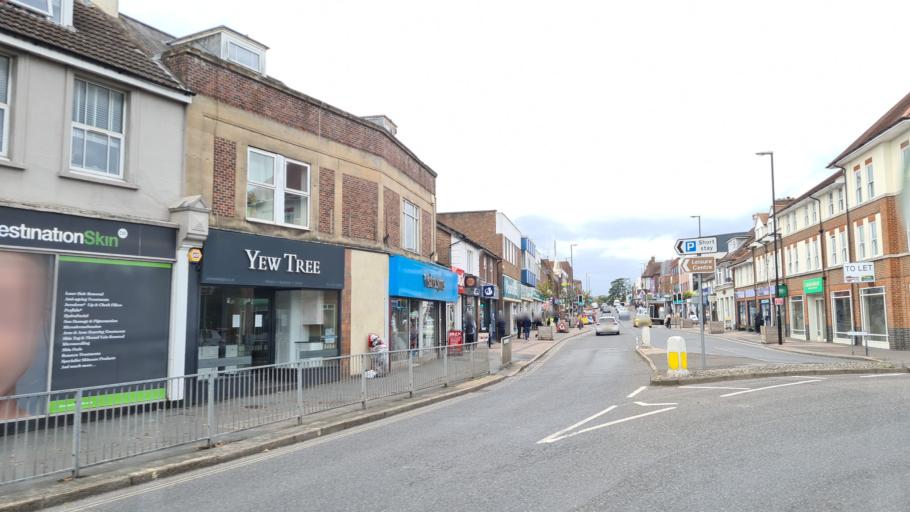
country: GB
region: England
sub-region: West Sussex
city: Haywards Heath
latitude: 50.9958
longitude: -0.1004
